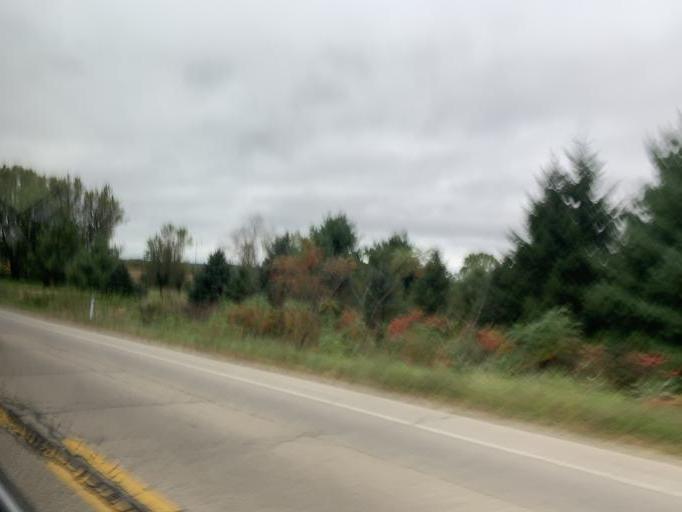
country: US
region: Wisconsin
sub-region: Grant County
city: Muscoda
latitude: 43.2099
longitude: -90.4581
